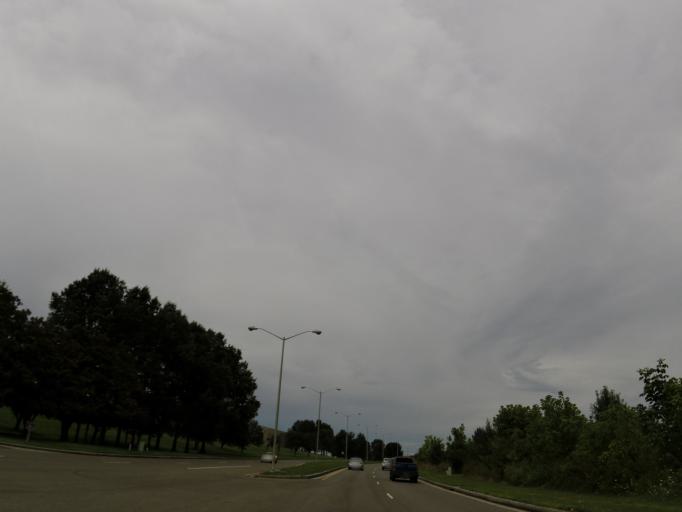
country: US
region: Tennessee
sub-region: Knox County
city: Farragut
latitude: 35.9036
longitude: -84.1366
